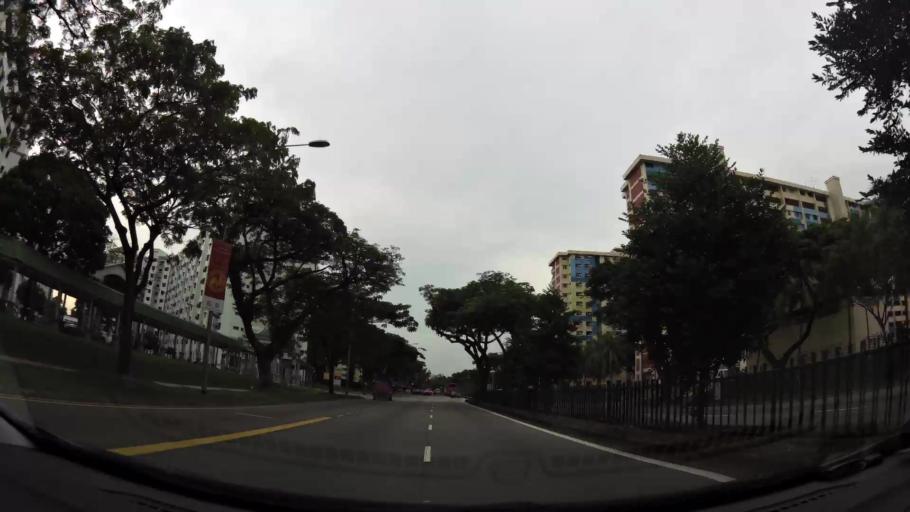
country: SG
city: Singapore
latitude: 1.3646
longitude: 103.8919
